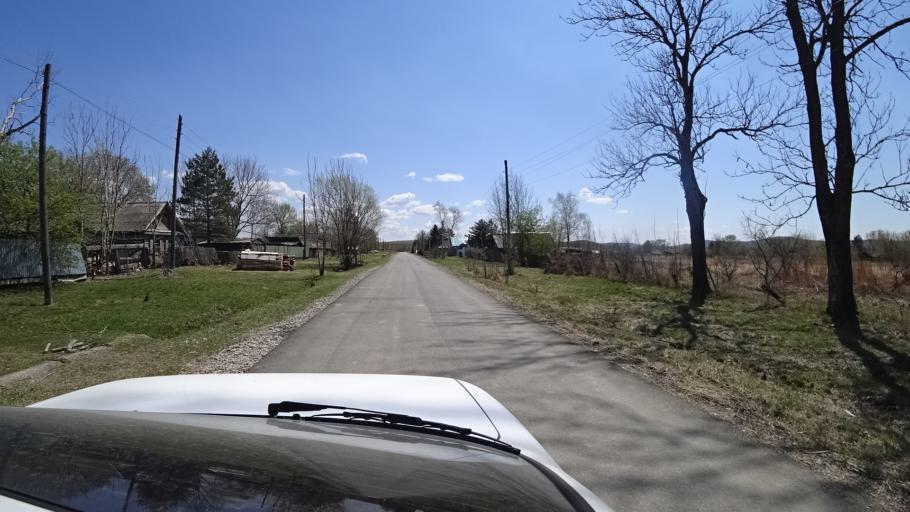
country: RU
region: Primorskiy
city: Dal'nerechensk
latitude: 45.7941
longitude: 133.7689
